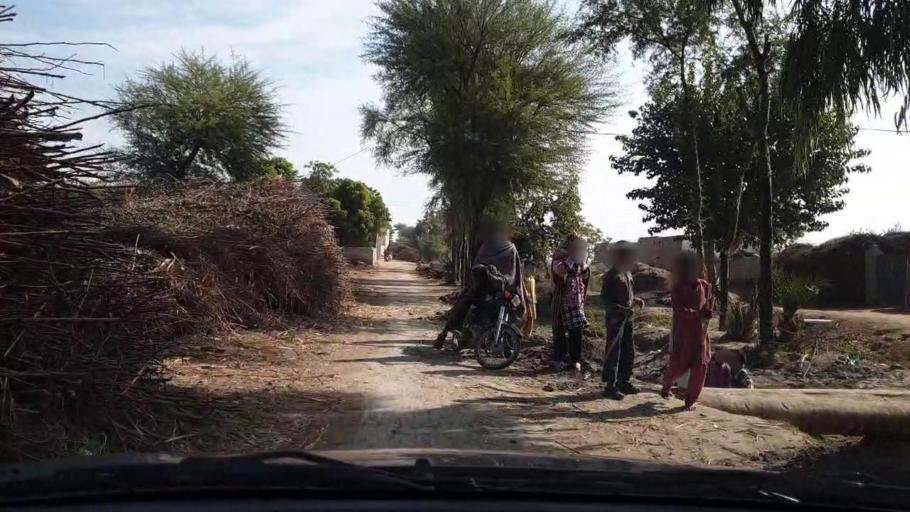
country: PK
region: Sindh
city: Jam Sahib
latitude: 26.2599
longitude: 68.7080
